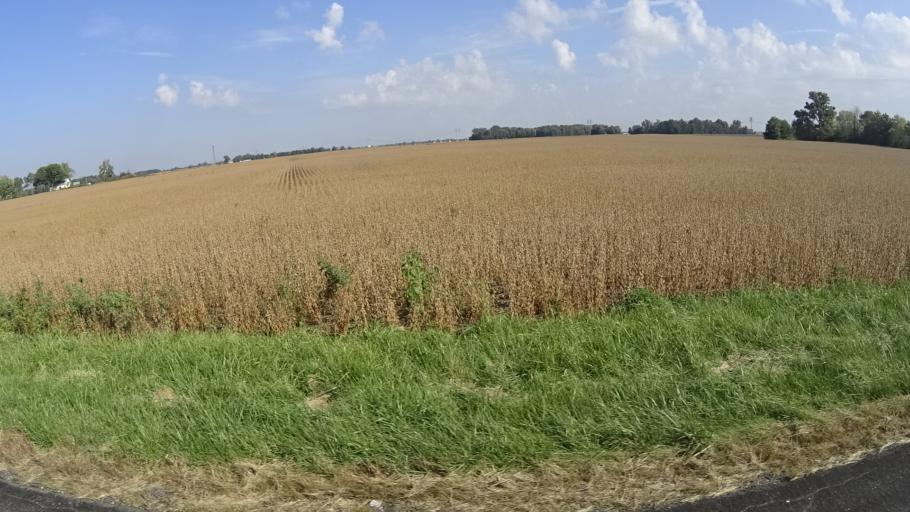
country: US
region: Indiana
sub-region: Madison County
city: Lapel
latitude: 40.0225
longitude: -85.8595
